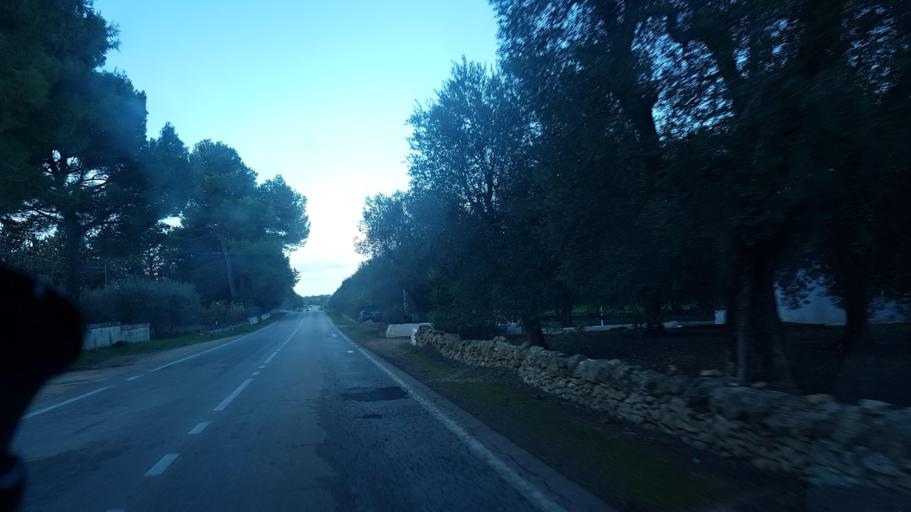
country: IT
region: Apulia
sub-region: Provincia di Brindisi
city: San Michele Salentino
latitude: 40.6655
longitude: 17.5991
